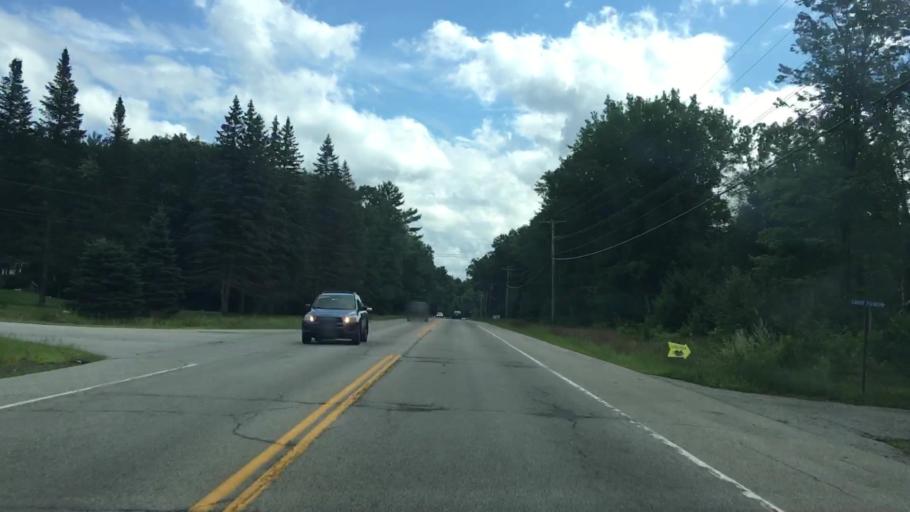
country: US
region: Maine
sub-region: York County
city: South Sanford
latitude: 43.4033
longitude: -70.7408
